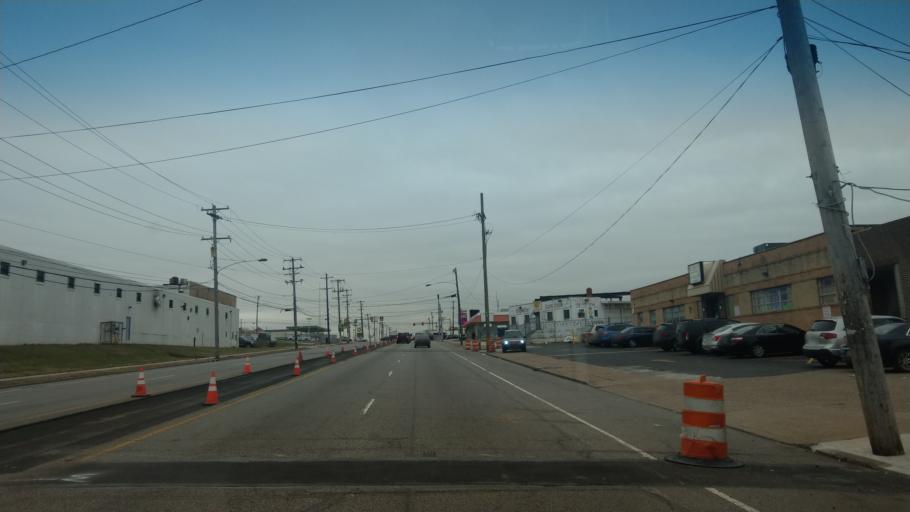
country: US
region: Pennsylvania
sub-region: Montgomery County
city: Rockledge
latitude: 40.0149
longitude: -75.1182
